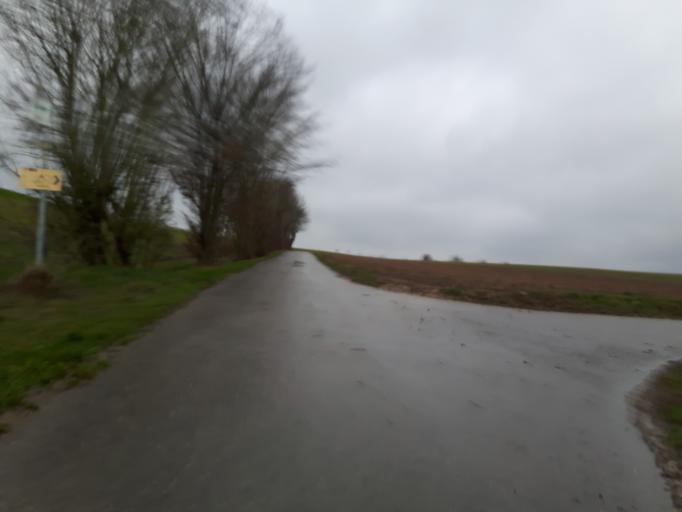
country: DE
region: Baden-Wuerttemberg
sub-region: Regierungsbezirk Stuttgart
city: Offenau
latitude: 49.2501
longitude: 9.1417
